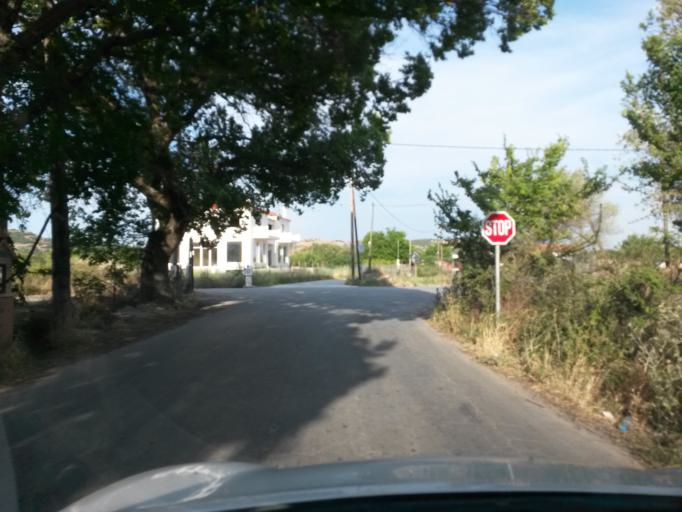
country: GR
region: North Aegean
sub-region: Nomos Lesvou
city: Kalloni
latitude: 39.2404
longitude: 26.2085
